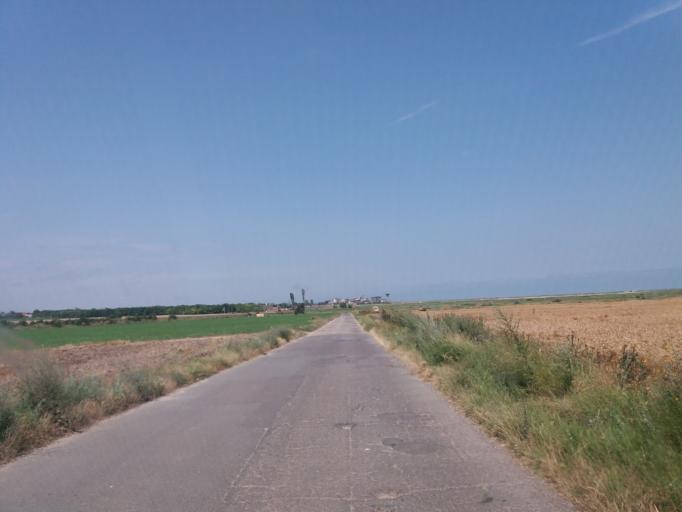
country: RO
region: Constanta
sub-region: Comuna Sacele
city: Sacele
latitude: 44.4366
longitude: 28.7240
